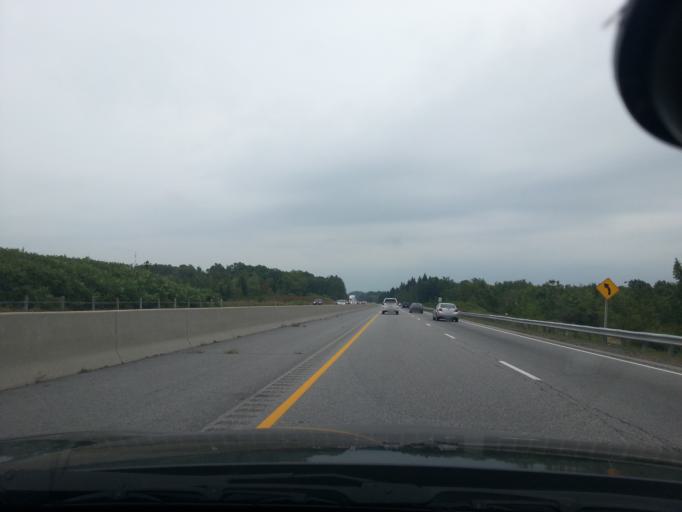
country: CA
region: Ontario
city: Gananoque
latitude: 44.3257
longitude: -76.2953
